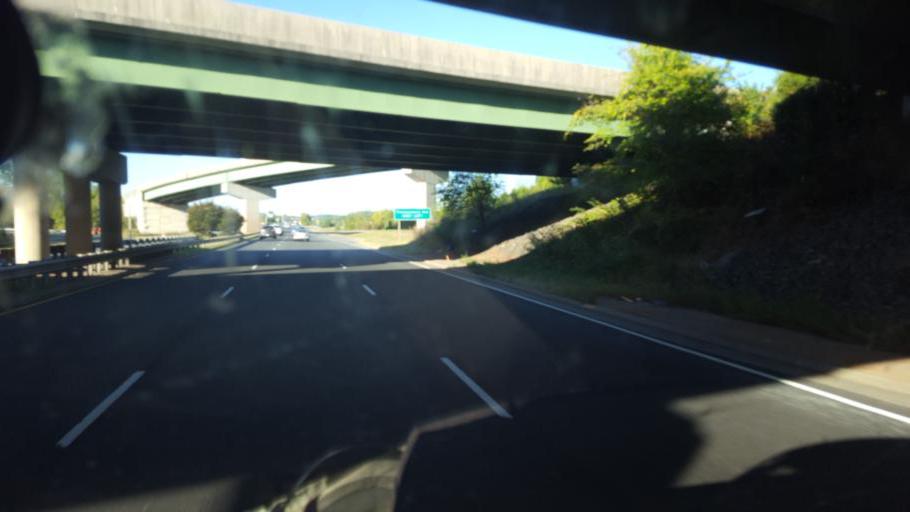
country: US
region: Virginia
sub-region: Prince William County
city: Bull Run
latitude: 38.7422
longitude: -77.5187
